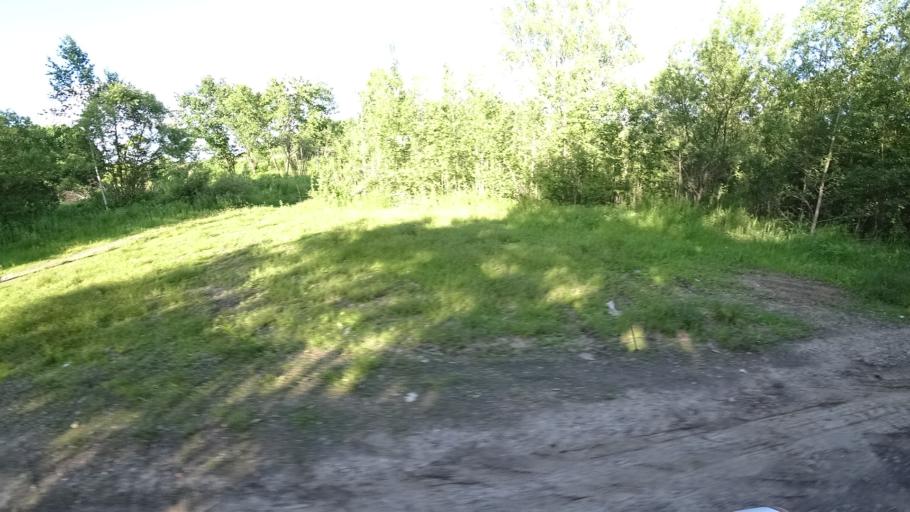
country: RU
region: Khabarovsk Krai
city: Khor
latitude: 47.8507
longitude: 134.9460
